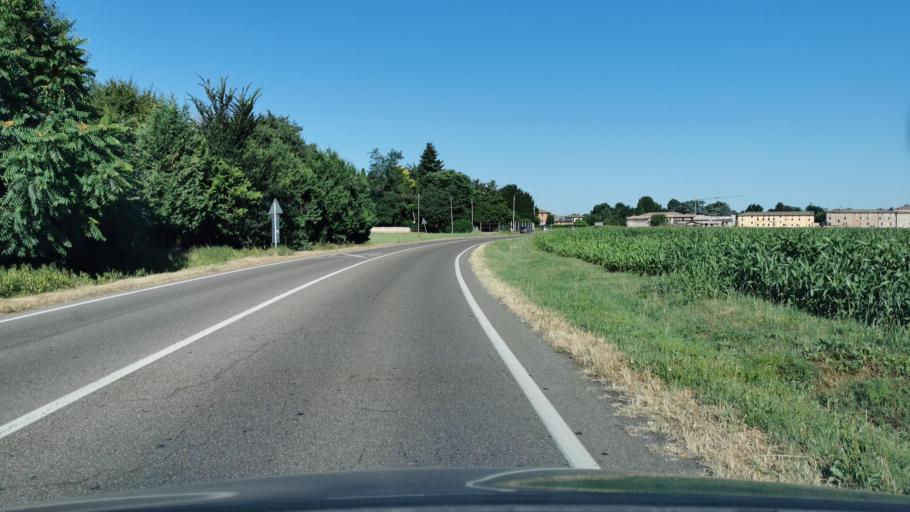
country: IT
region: Emilia-Romagna
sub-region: Provincia di Modena
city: Baggiovara
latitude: 44.6195
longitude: 10.8958
